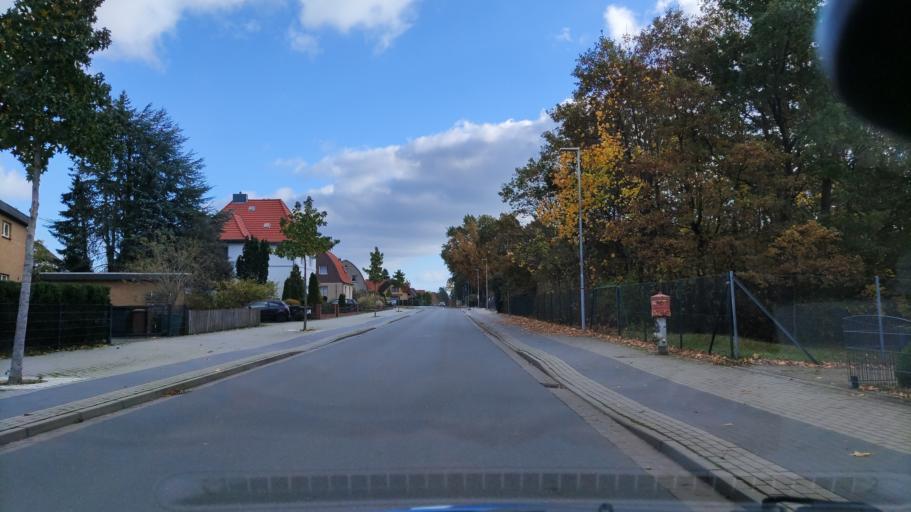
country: DE
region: Lower Saxony
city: Munster
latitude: 52.9866
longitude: 10.0986
